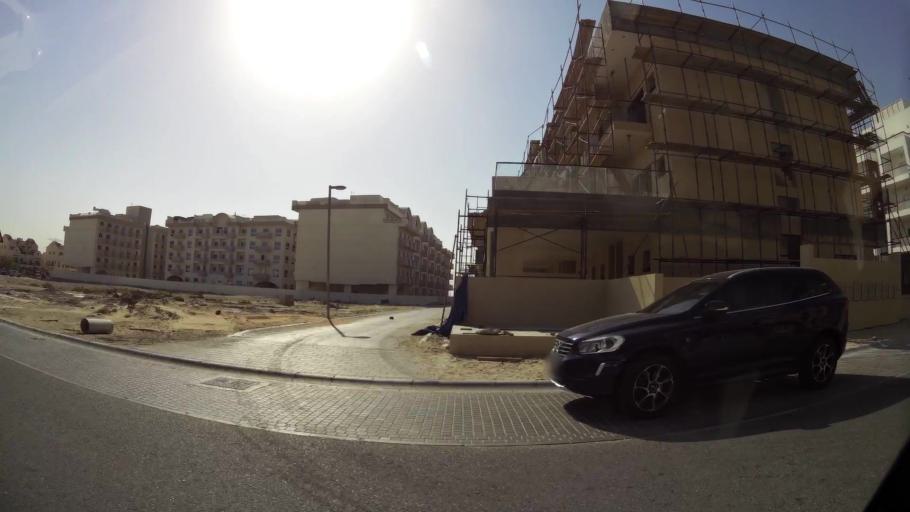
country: AE
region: Dubai
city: Dubai
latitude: 25.0683
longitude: 55.2064
